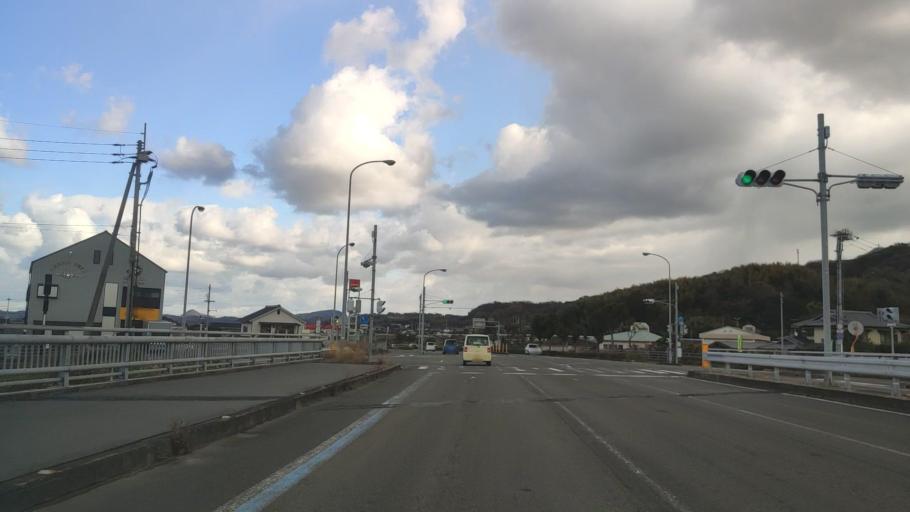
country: JP
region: Ehime
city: Hojo
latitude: 33.9356
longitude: 132.7710
